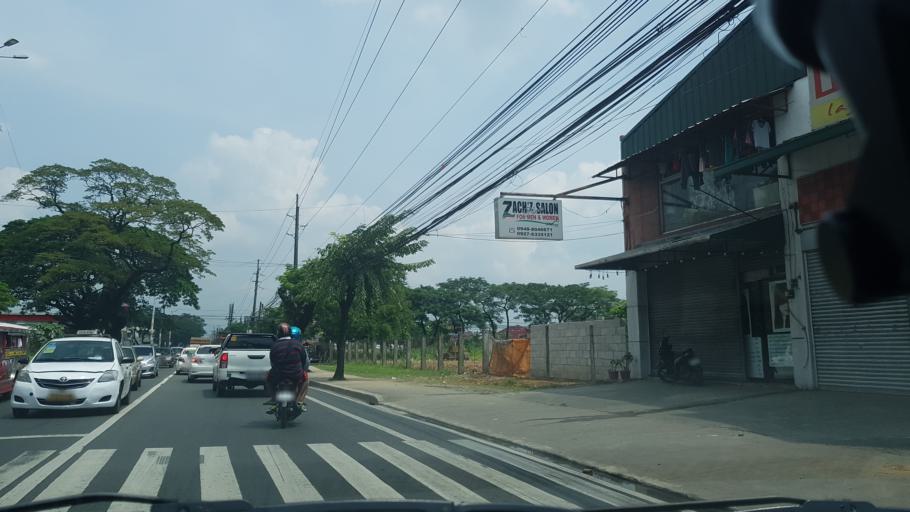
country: PH
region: Calabarzon
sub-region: Province of Rizal
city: San Mateo
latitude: 14.6643
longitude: 121.1066
